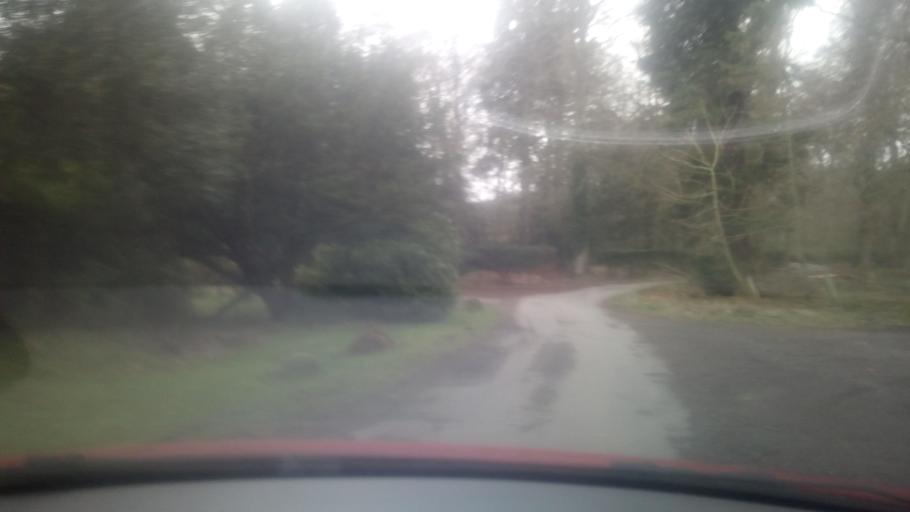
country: GB
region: Scotland
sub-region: The Scottish Borders
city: Jedburgh
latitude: 55.4460
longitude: -2.6406
